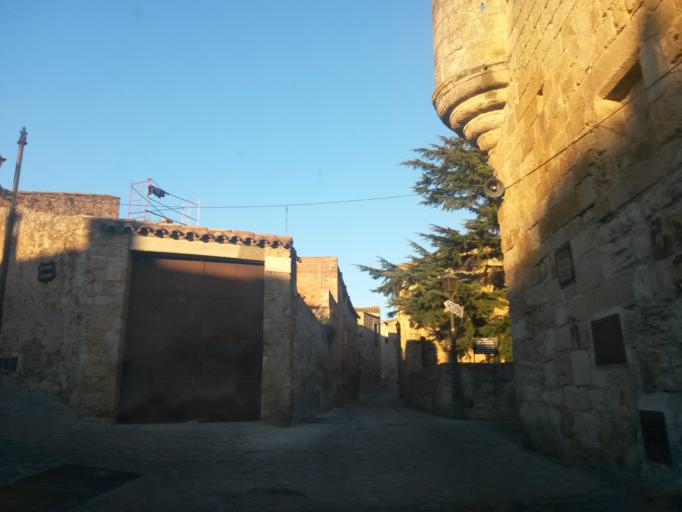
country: ES
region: Catalonia
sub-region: Provincia de Girona
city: Pals
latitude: 41.9706
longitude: 3.1444
